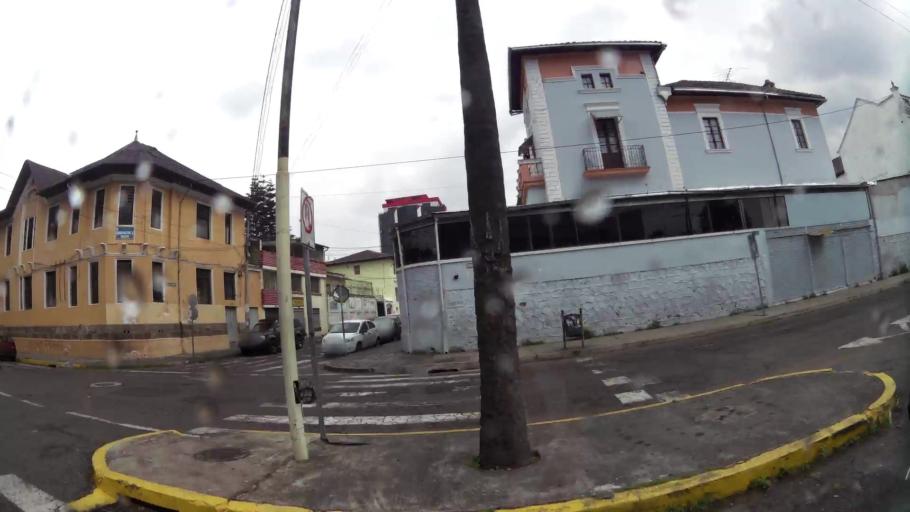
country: EC
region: Pichincha
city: Quito
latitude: -0.2134
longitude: -78.4995
